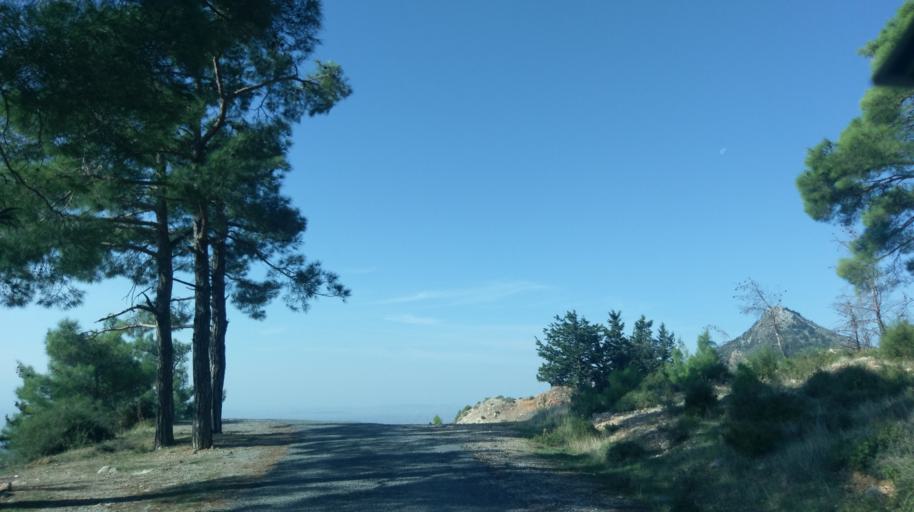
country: CY
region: Keryneia
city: Kyrenia
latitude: 35.2837
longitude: 33.4014
